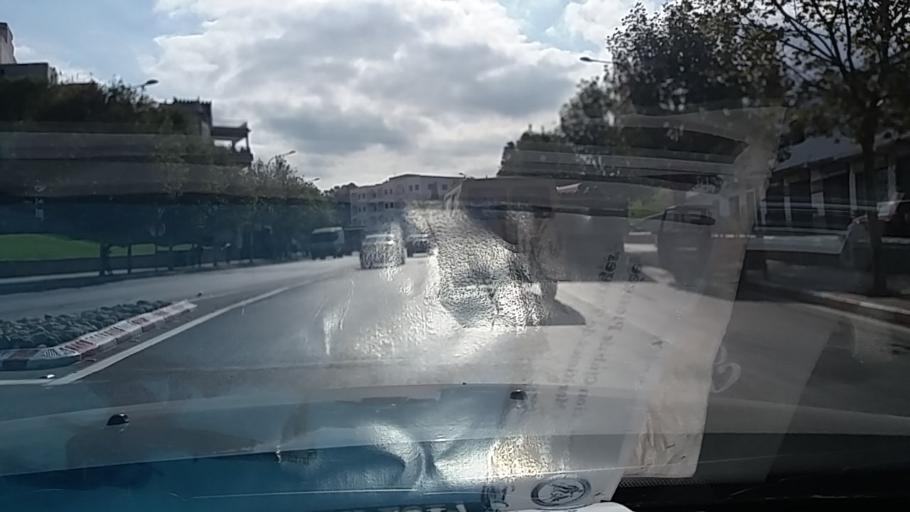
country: MA
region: Tanger-Tetouan
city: Tetouan
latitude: 35.5653
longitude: -5.3979
